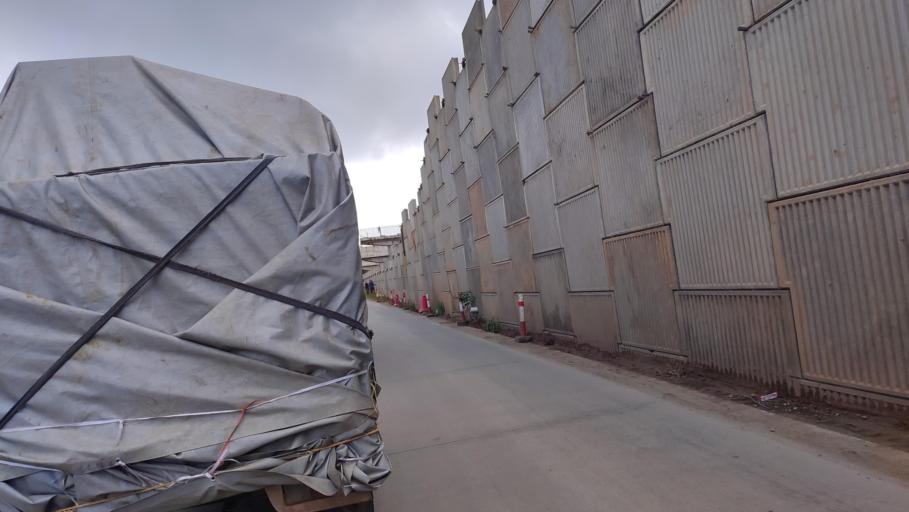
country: IN
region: Kerala
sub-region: Kasaragod District
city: Nileshwar
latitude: 12.2428
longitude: 75.1469
